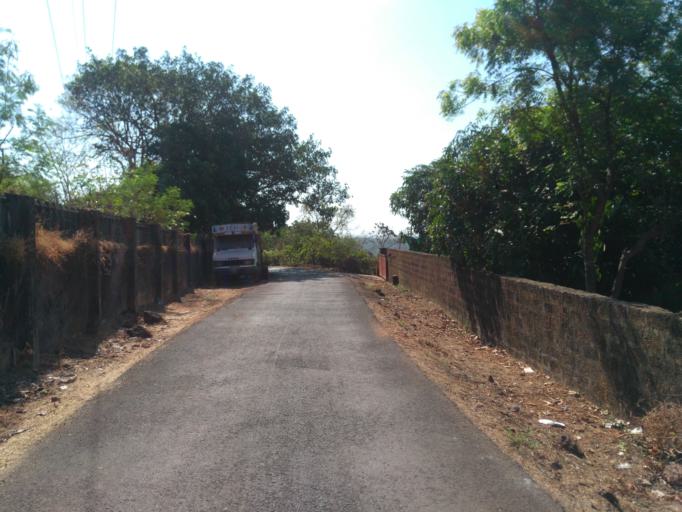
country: IN
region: Maharashtra
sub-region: Ratnagiri
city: Ratnagiri
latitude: 16.9822
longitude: 73.3119
